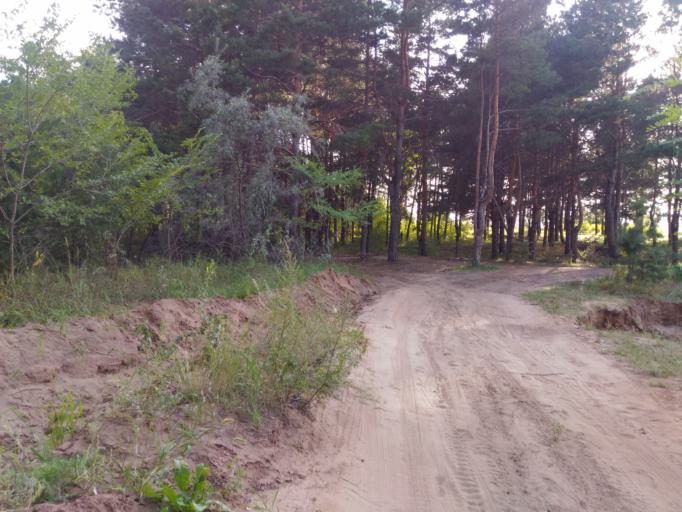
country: RU
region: Ulyanovsk
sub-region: Ulyanovskiy Rayon
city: Ulyanovsk
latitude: 54.3545
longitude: 48.5158
